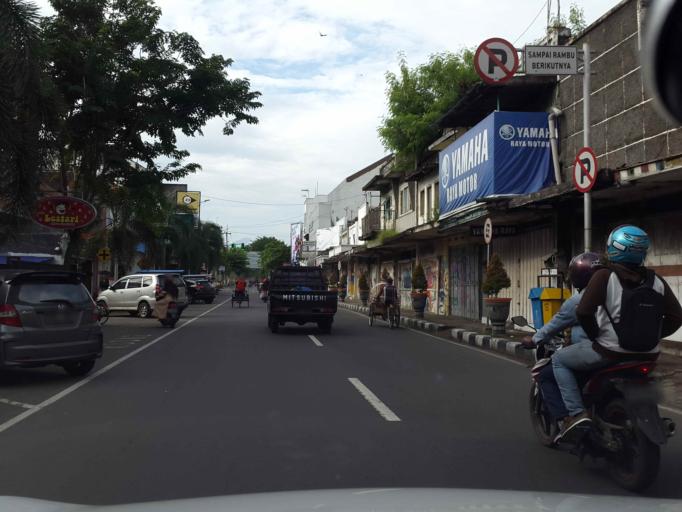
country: ID
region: East Java
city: Mojokerto
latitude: -7.4702
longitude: 112.4319
